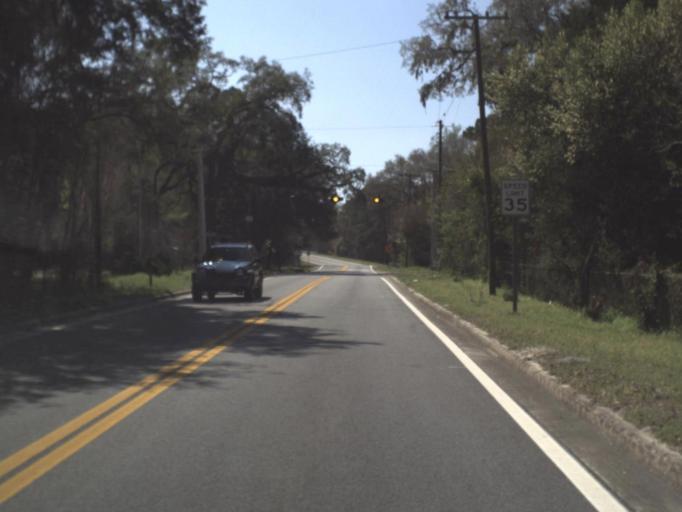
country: US
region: Florida
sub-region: Jefferson County
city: Monticello
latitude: 30.4788
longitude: -84.0226
